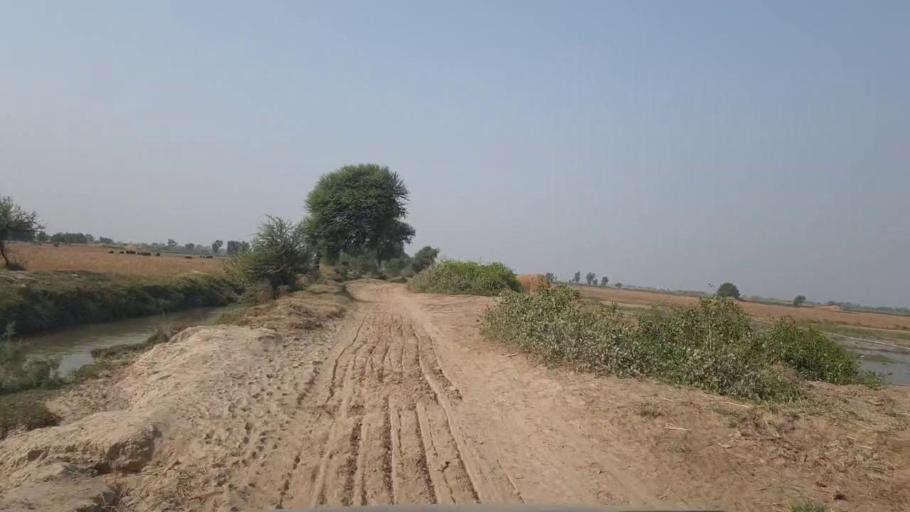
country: PK
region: Sindh
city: Tando Muhammad Khan
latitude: 25.0704
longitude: 68.3571
